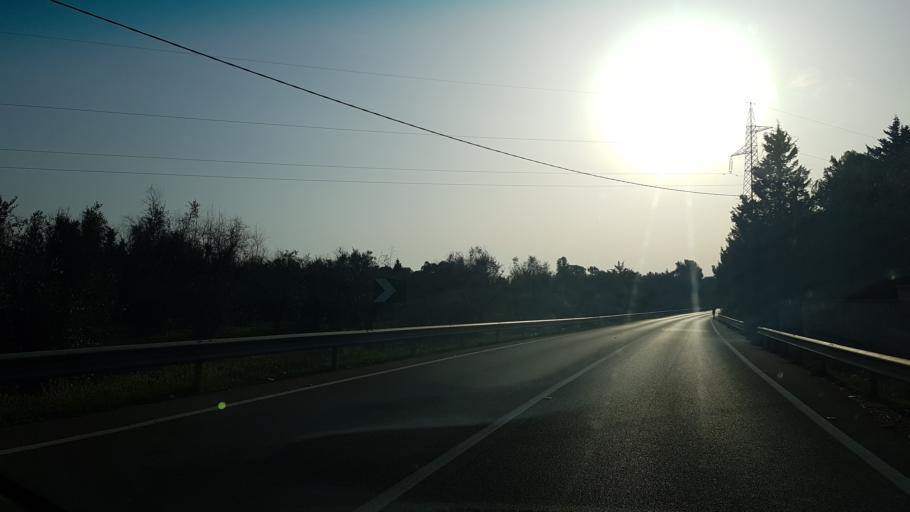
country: IT
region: Apulia
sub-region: Provincia di Lecce
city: Trepuzzi
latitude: 40.3992
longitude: 18.0592
